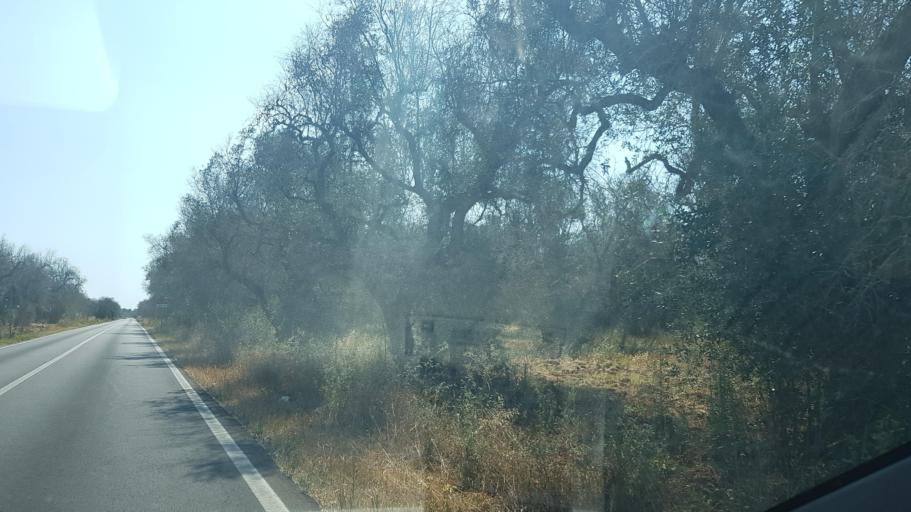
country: IT
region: Apulia
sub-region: Provincia di Lecce
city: Ruffano
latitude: 40.0026
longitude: 18.2837
